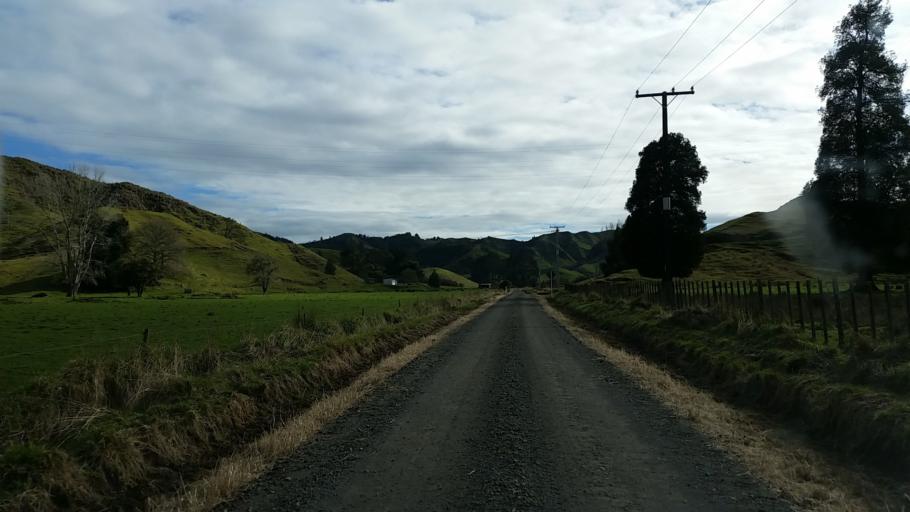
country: NZ
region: Taranaki
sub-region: South Taranaki District
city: Eltham
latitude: -39.2337
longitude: 174.5683
